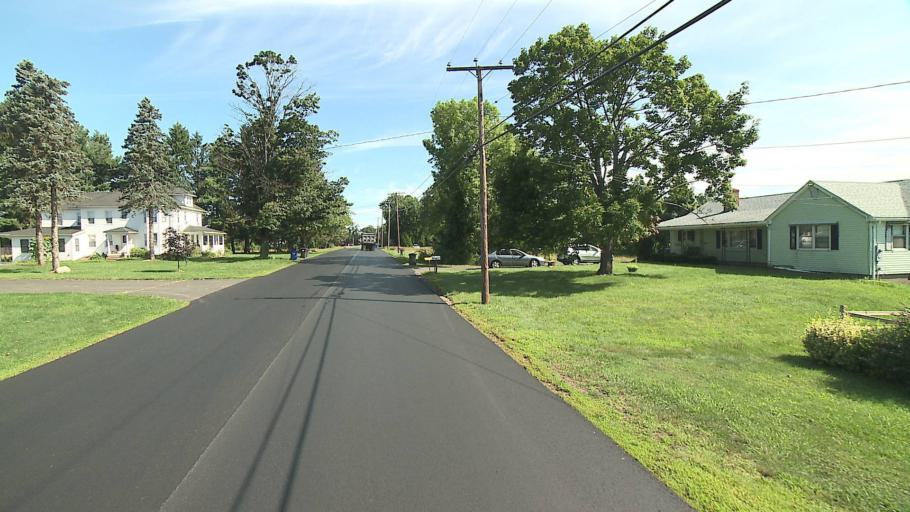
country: US
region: Connecticut
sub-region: Hartford County
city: Suffield Depot
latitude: 41.9839
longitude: -72.7057
